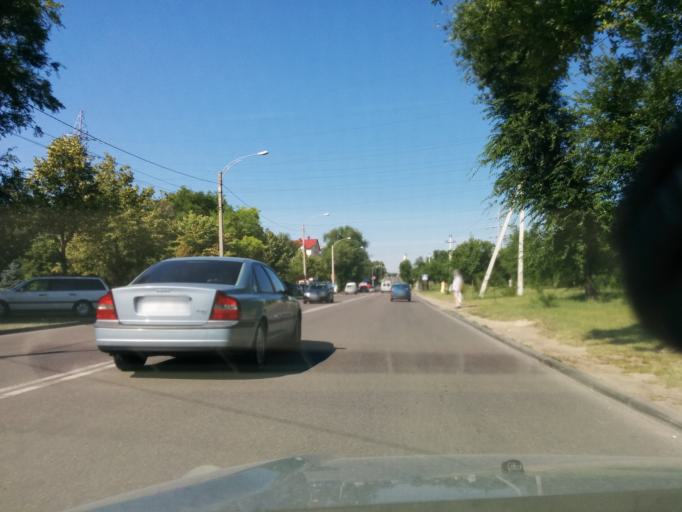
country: MD
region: Chisinau
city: Chisinau
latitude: 47.0324
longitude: 28.8870
